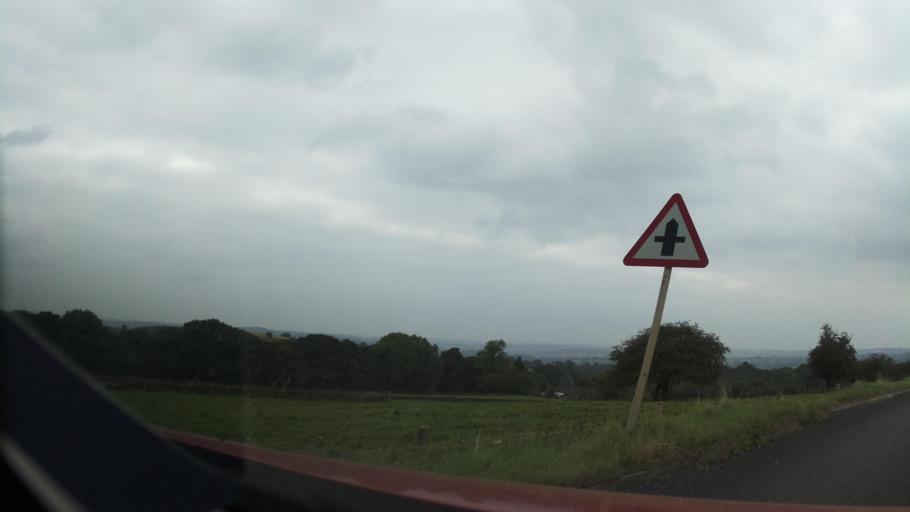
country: GB
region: England
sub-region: Staffordshire
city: Cheadle
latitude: 53.0308
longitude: -1.9199
